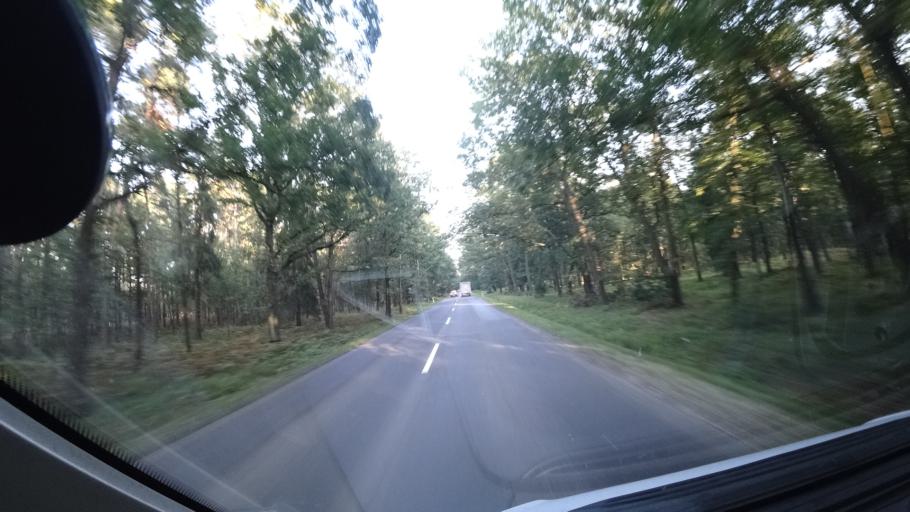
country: PL
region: Silesian Voivodeship
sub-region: Powiat gliwicki
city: Rudziniec
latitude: 50.2747
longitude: 18.3854
